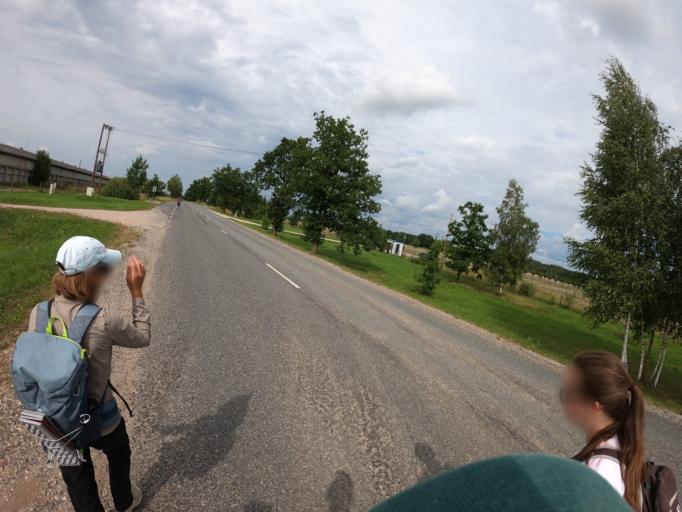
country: LV
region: Aizpute
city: Aizpute
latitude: 56.6975
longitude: 21.6316
